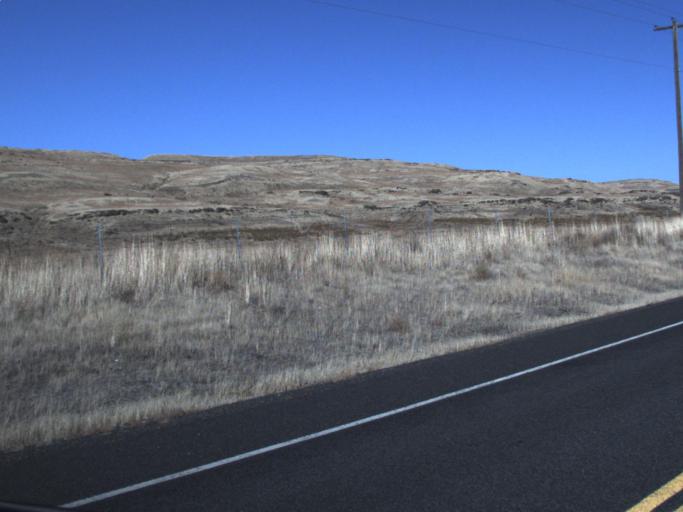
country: US
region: Washington
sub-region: Adams County
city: Ritzville
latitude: 46.6976
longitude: -118.4206
